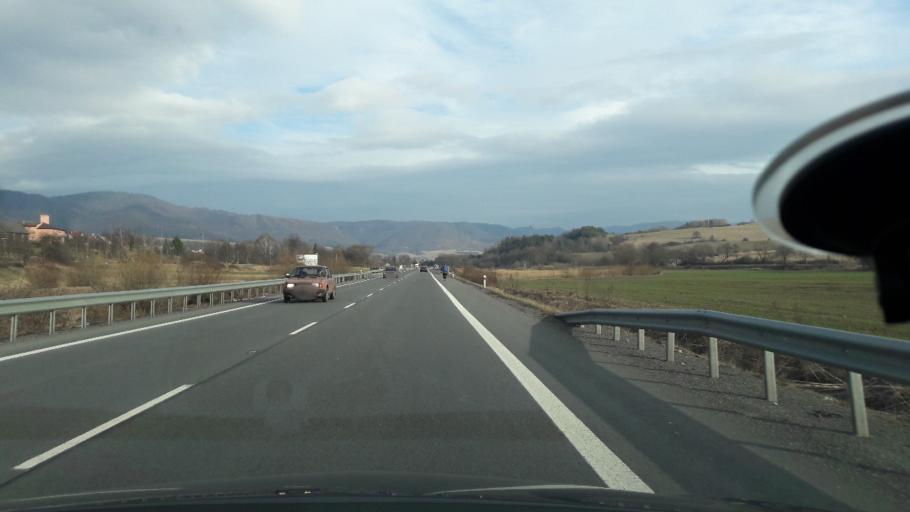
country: SK
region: Nitriansky
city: Handlova
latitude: 48.7783
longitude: 18.7048
